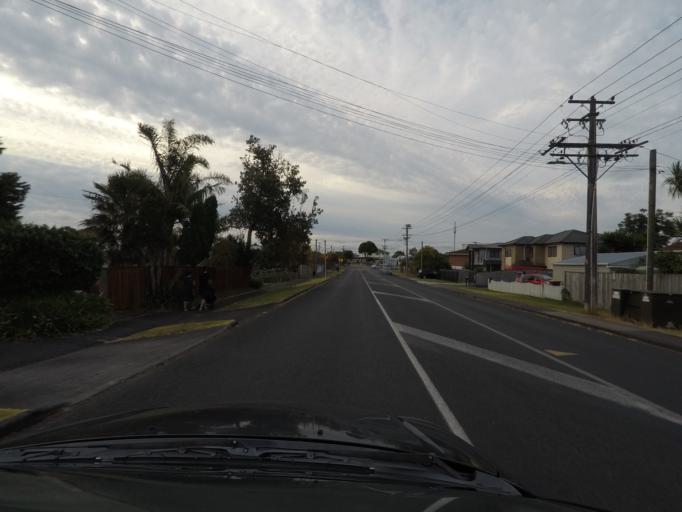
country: NZ
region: Auckland
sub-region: Auckland
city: Rosebank
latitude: -36.8325
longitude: 174.6479
